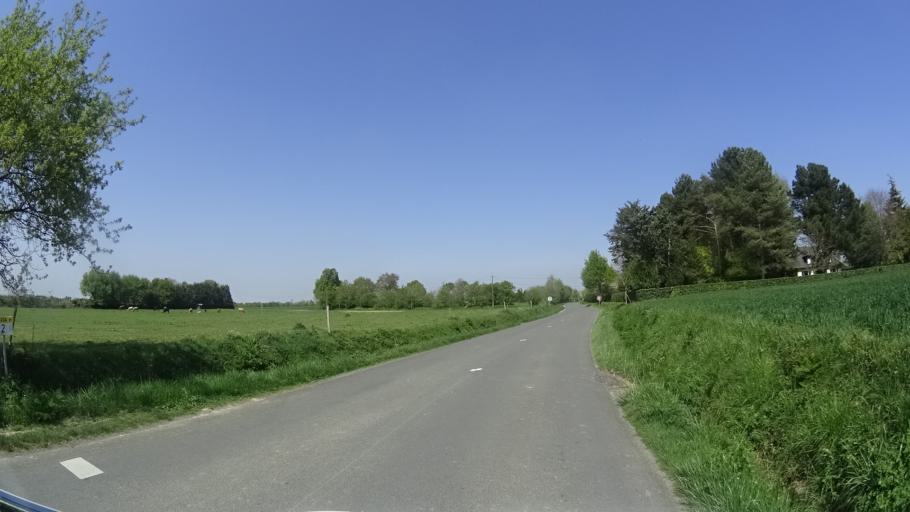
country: FR
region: Brittany
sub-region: Departement d'Ille-et-Vilaine
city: Chavagne
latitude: 48.0700
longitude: -1.7933
